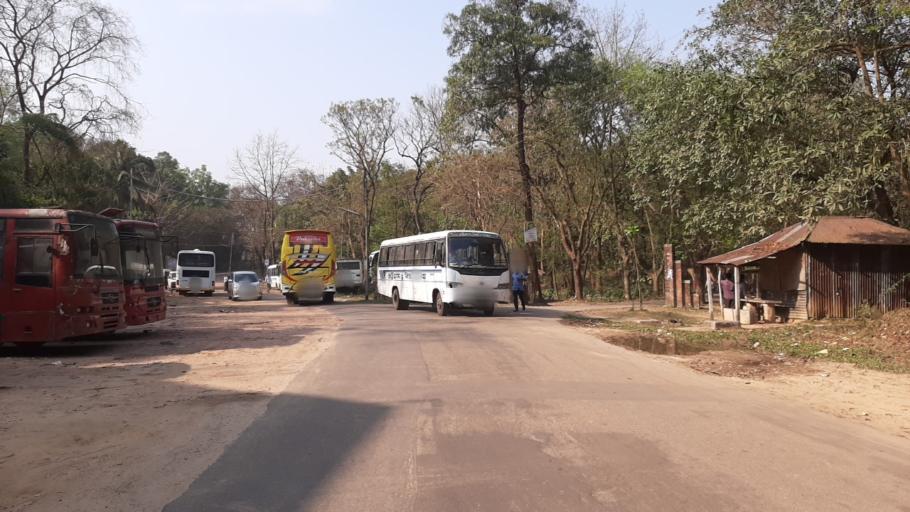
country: BD
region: Chittagong
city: Raojan
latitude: 22.4758
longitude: 91.7916
